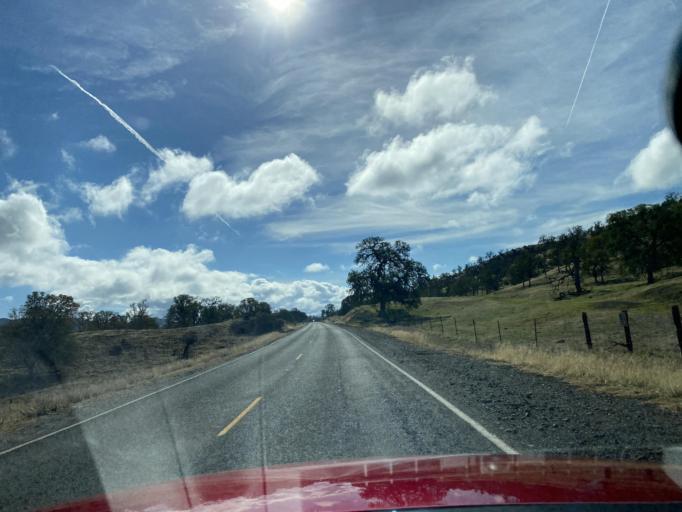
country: US
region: California
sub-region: Glenn County
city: Willows
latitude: 39.4918
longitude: -122.5206
